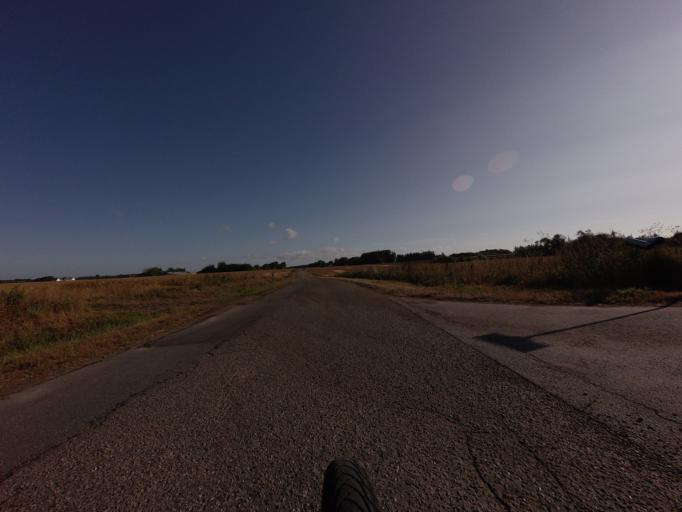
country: DK
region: North Denmark
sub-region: Hjorring Kommune
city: Vra
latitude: 57.3901
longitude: 9.9513
